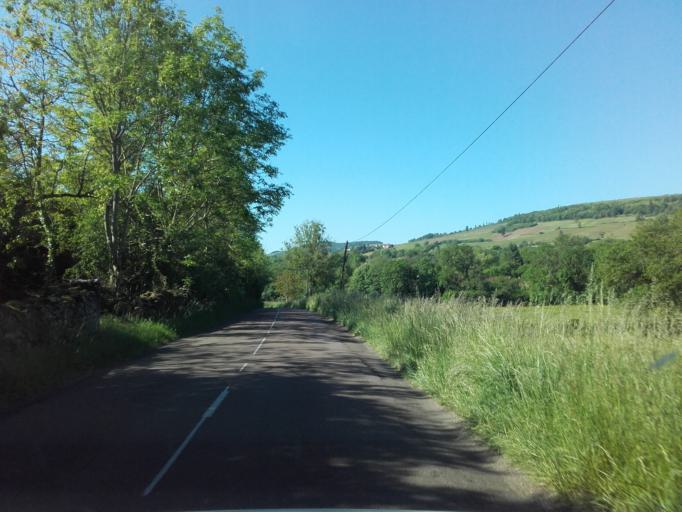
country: FR
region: Bourgogne
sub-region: Departement de la Cote-d'Or
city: Nolay
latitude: 46.9434
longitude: 4.6290
